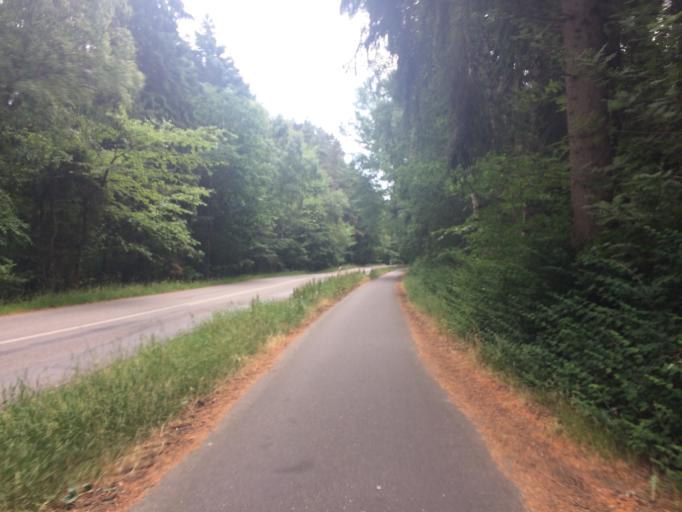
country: DK
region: Capital Region
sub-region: Bornholm Kommune
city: Ronne
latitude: 55.1667
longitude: 14.7144
